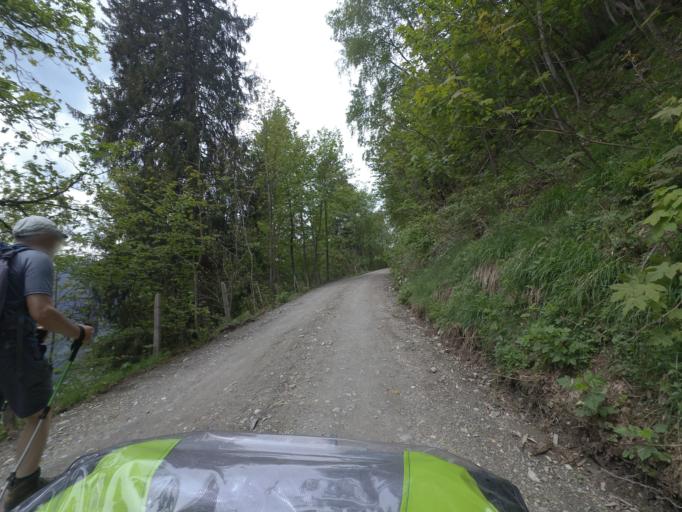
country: AT
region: Salzburg
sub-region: Politischer Bezirk Sankt Johann im Pongau
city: Dorfgastein
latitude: 47.2544
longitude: 13.1218
